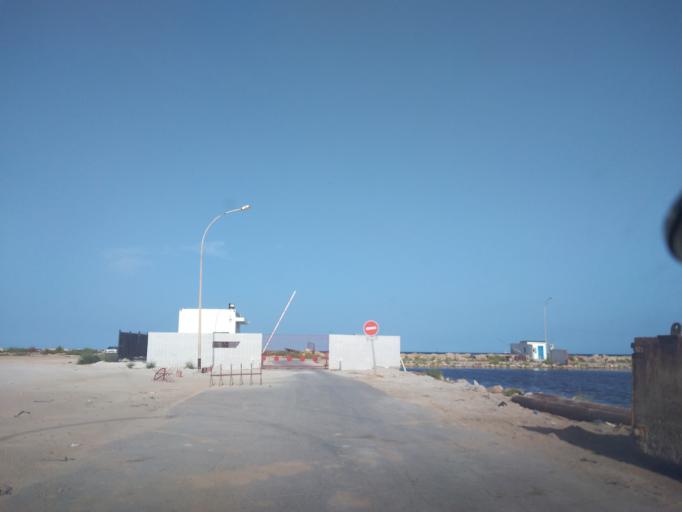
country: TN
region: Safaqis
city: Sfax
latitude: 34.7171
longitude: 10.7690
